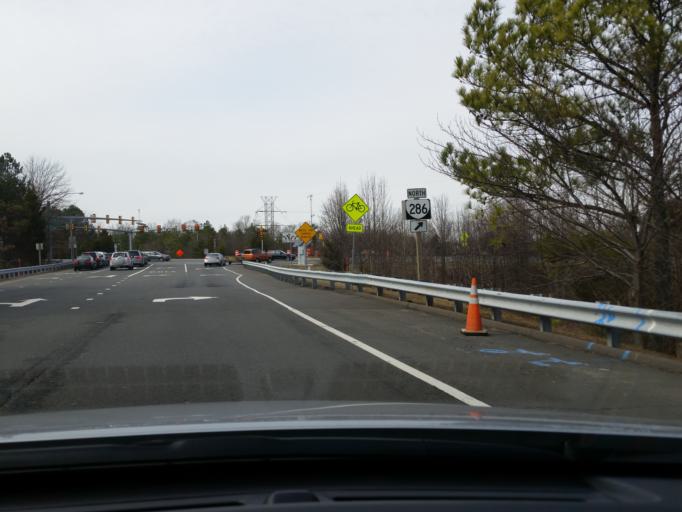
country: US
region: Virginia
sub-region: Fairfax County
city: Herndon
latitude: 38.9540
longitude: -77.3720
